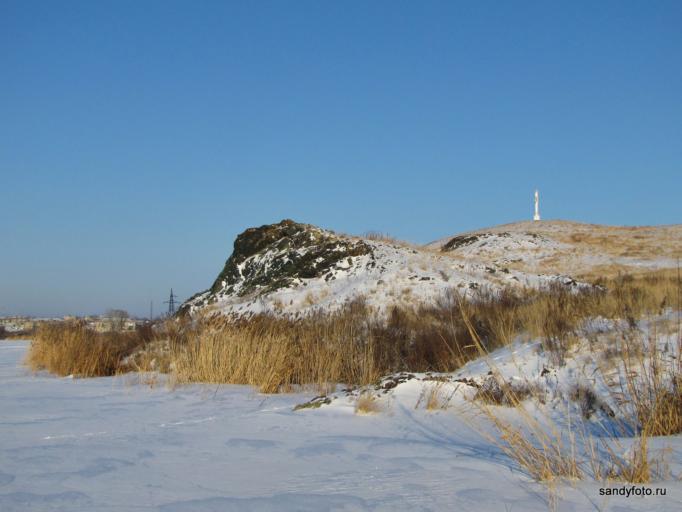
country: RU
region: Chelyabinsk
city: Troitsk
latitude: 54.0767
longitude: 61.5775
